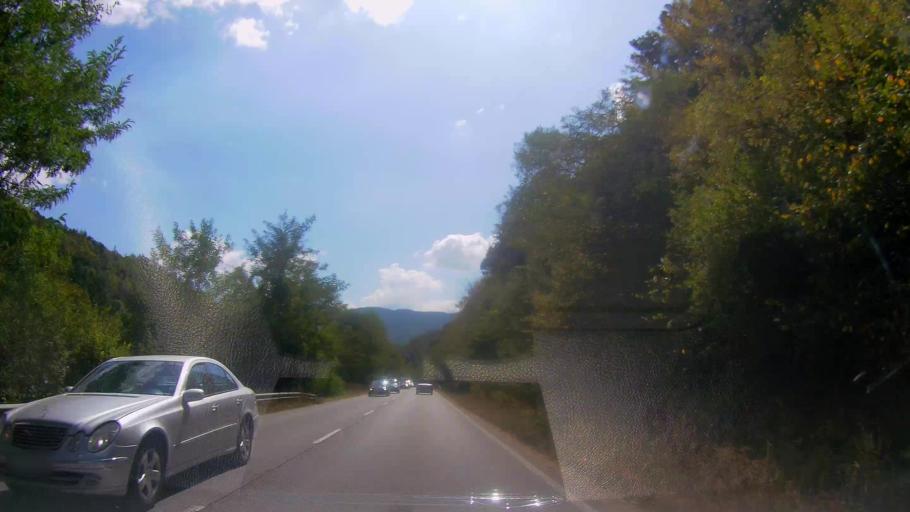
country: BG
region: Stara Zagora
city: Gurkovo
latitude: 42.7294
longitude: 25.7122
